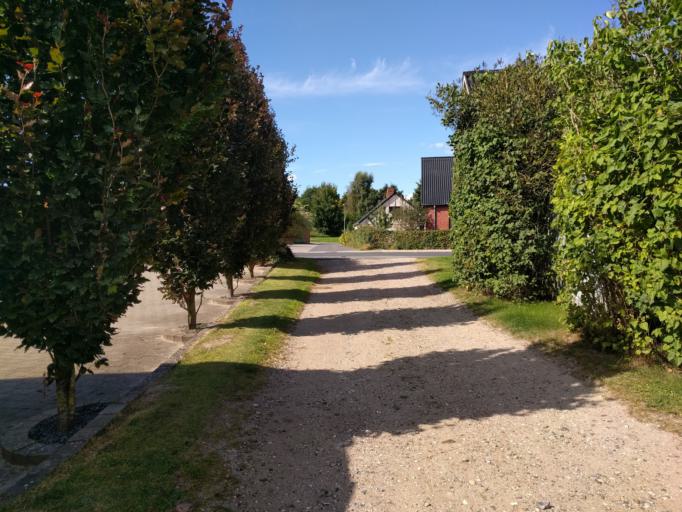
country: DK
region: Central Jutland
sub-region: Viborg Kommune
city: Bjerringbro
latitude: 56.5296
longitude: 9.5773
